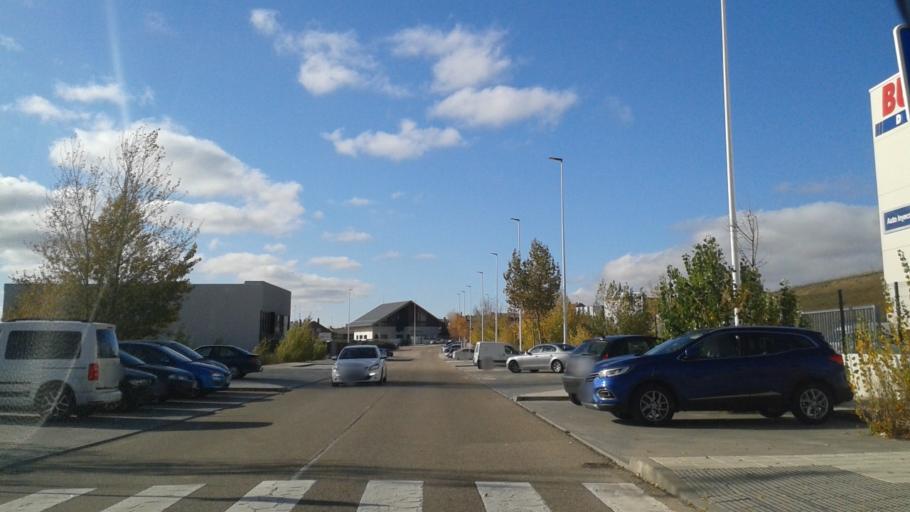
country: ES
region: Castille and Leon
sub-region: Provincia de Valladolid
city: Arroyo
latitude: 41.6278
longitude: -4.7643
